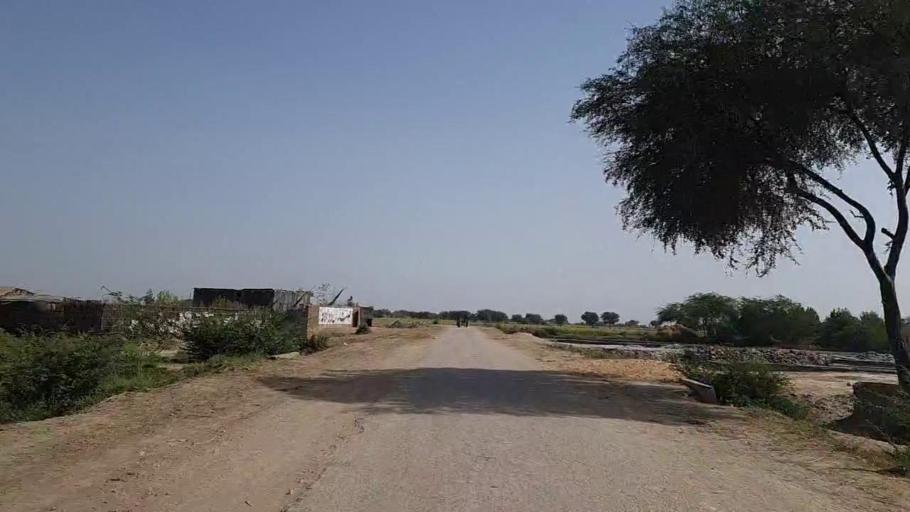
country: PK
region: Sindh
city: Jati
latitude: 24.3547
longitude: 68.2748
